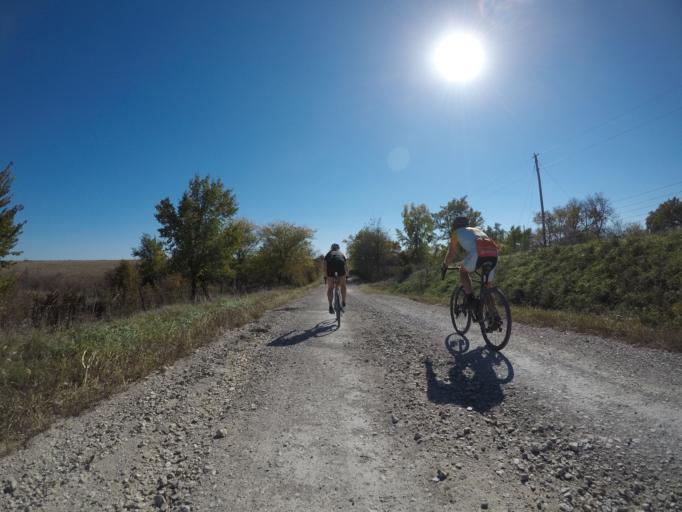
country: US
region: Kansas
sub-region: Wabaunsee County
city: Alma
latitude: 38.9590
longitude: -96.4734
